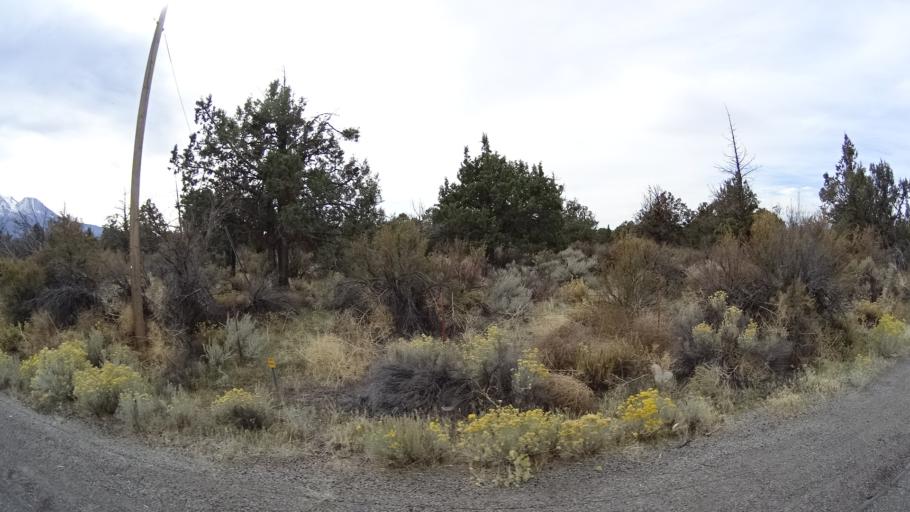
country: US
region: California
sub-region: Siskiyou County
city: Weed
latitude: 41.5807
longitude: -122.2895
